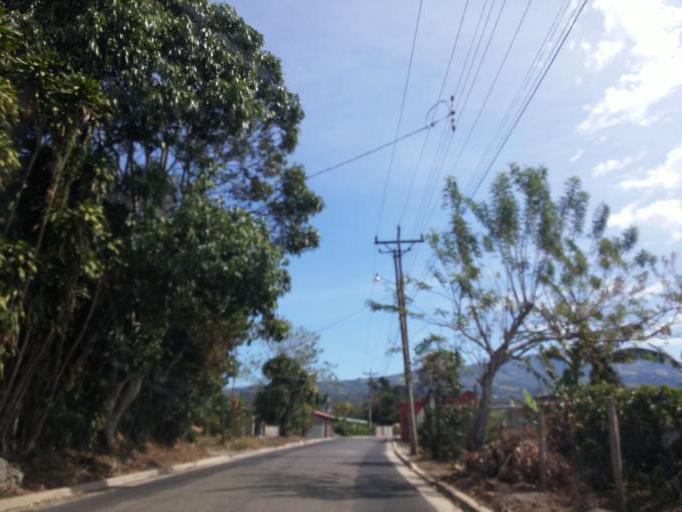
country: CR
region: Alajuela
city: Sabanilla
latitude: 10.0711
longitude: -84.2057
